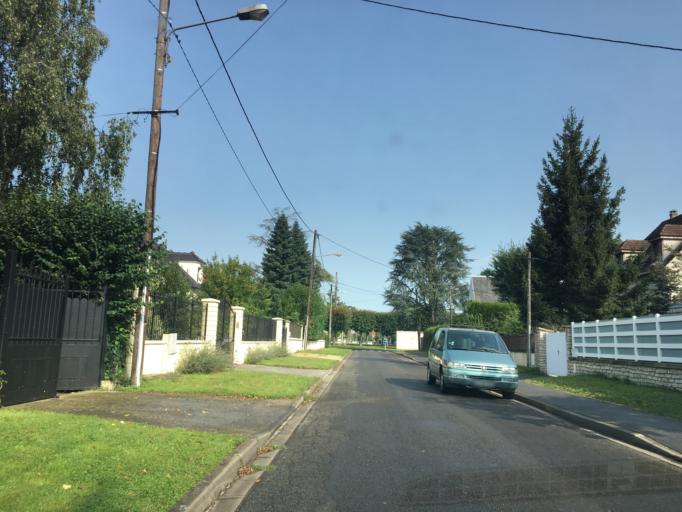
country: FR
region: Ile-de-France
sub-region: Departement de Seine-et-Marne
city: Gretz-Armainvilliers
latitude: 48.7373
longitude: 2.7173
